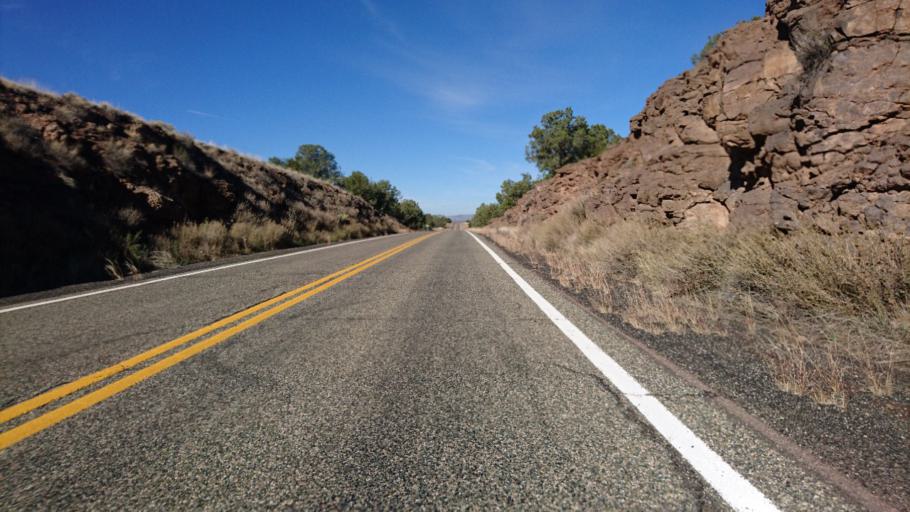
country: US
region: Arizona
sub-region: Yavapai County
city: Paulden
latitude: 35.2803
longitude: -112.7046
